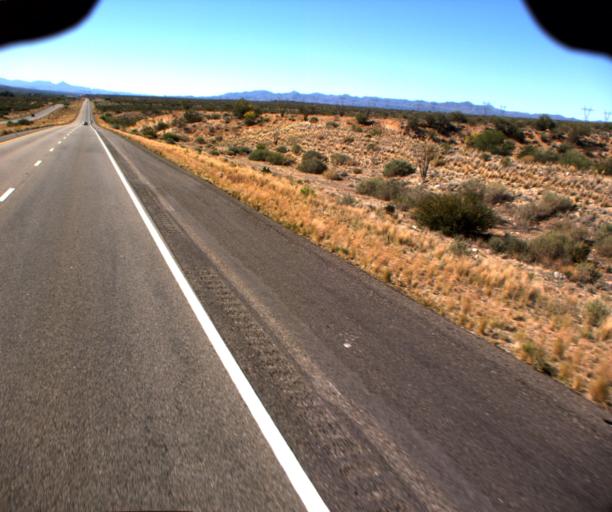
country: US
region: Arizona
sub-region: Mohave County
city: Kingman
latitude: 34.8617
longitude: -113.6419
